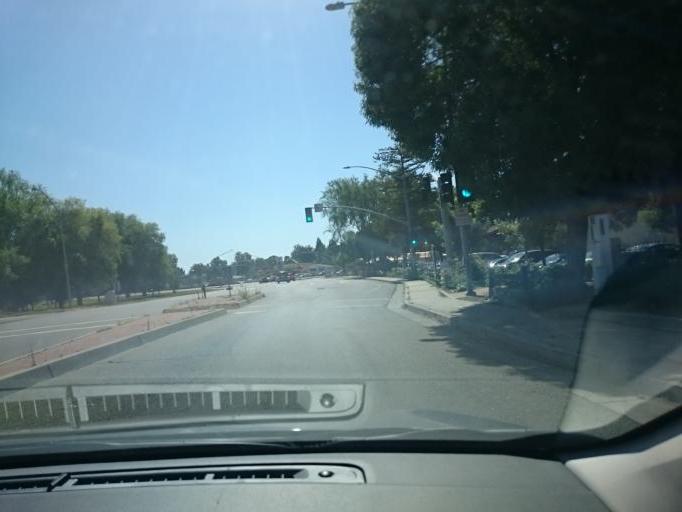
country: US
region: California
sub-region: Yolo County
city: Davis
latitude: 38.5506
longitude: -121.6964
